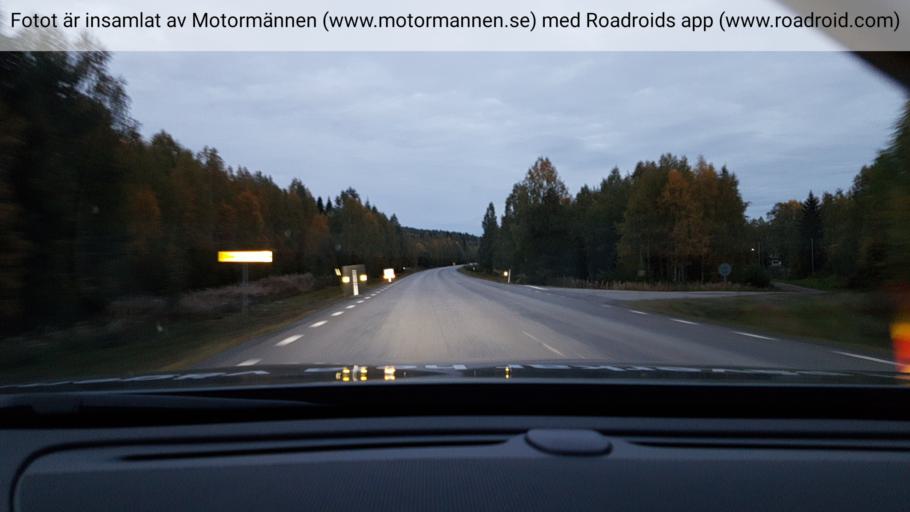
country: SE
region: Norrbotten
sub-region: Alvsbyns Kommun
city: AElvsbyn
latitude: 65.7821
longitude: 20.8047
